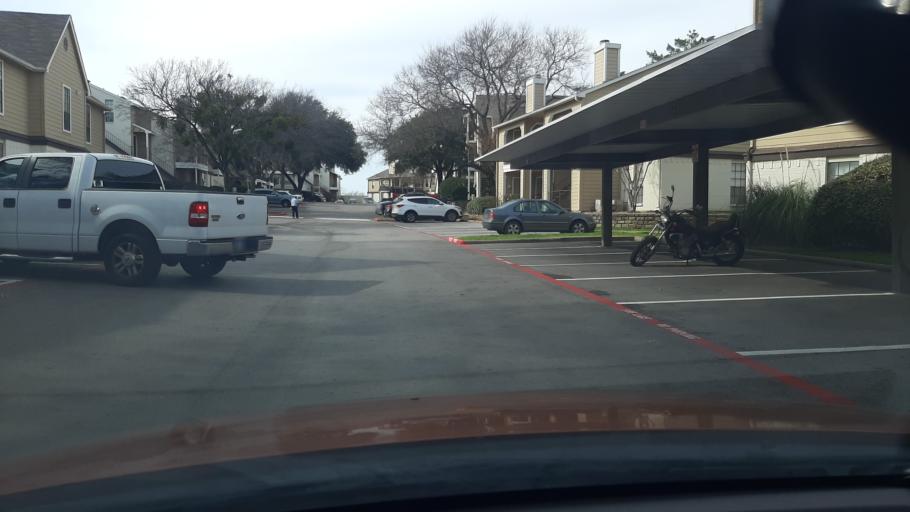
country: US
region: Texas
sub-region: Tarrant County
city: Benbrook
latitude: 32.6624
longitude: -97.4088
